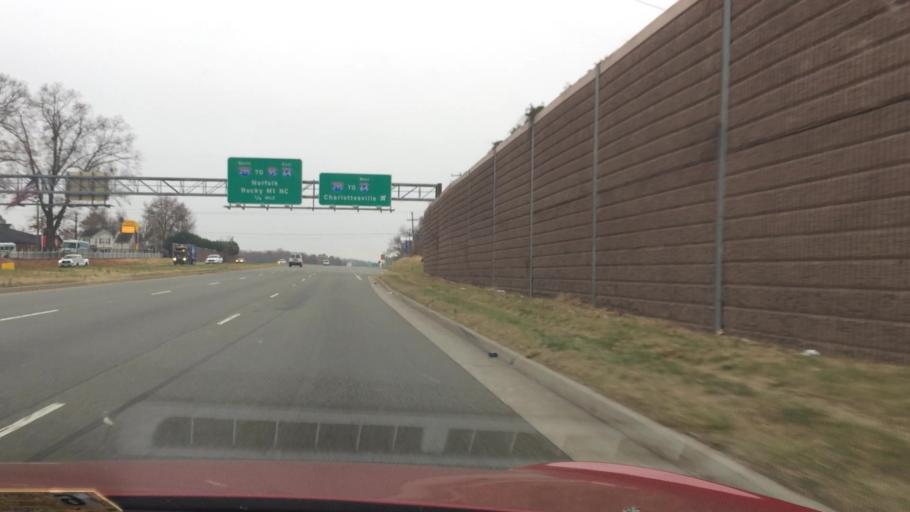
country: US
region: Virginia
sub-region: Henrico County
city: Glen Allen
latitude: 37.6646
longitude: -77.4606
